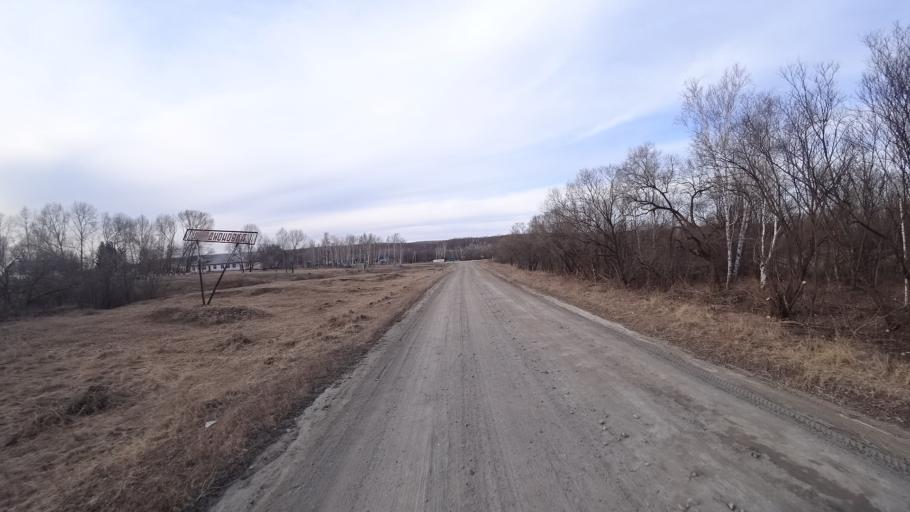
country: RU
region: Amur
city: Bureya
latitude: 50.0180
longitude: 129.7732
